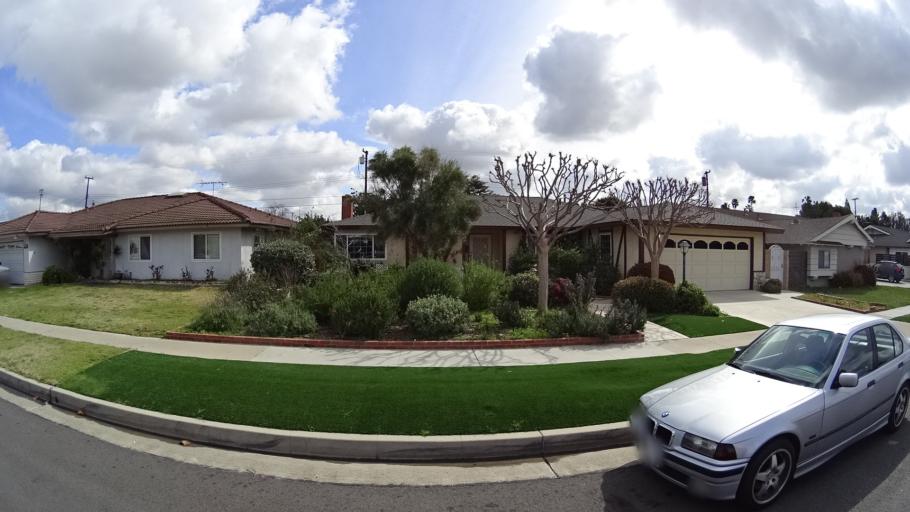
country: US
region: California
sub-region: Orange County
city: Buena Park
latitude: 33.8382
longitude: -117.9747
